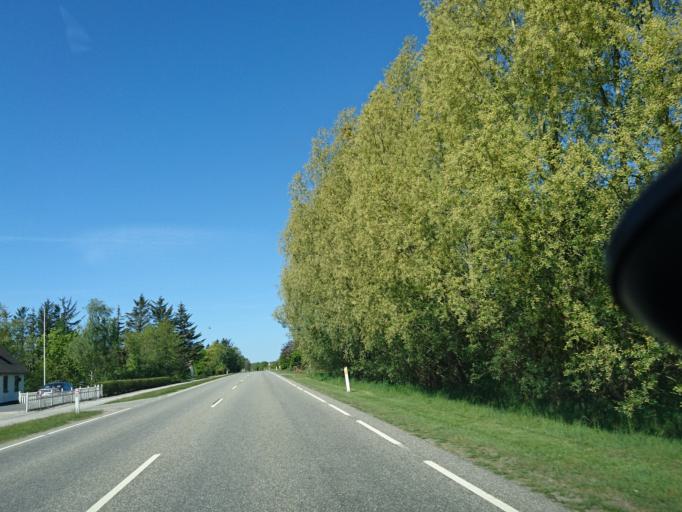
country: DK
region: North Denmark
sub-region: Hjorring Kommune
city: Sindal
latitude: 57.4693
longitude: 10.2424
